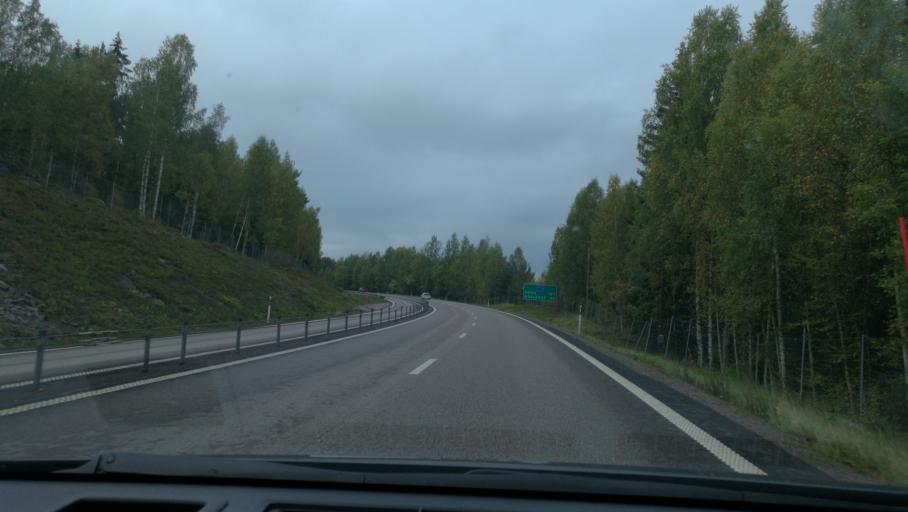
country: SE
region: Dalarna
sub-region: Saters Kommun
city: Saeter
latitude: 60.3567
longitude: 15.7450
